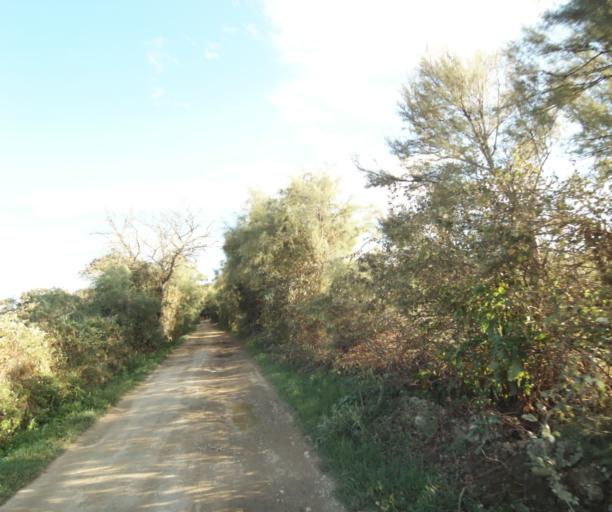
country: FR
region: Languedoc-Roussillon
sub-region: Departement des Pyrenees-Orientales
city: Argelers
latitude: 42.5667
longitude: 3.0207
